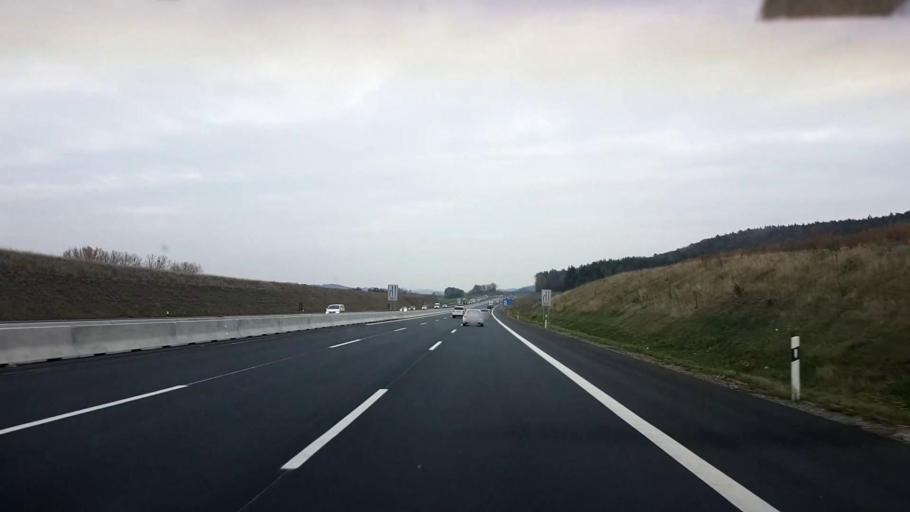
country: DE
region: Bavaria
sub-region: Regierungsbezirk Unterfranken
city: Geiselwind
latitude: 49.7691
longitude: 10.4834
